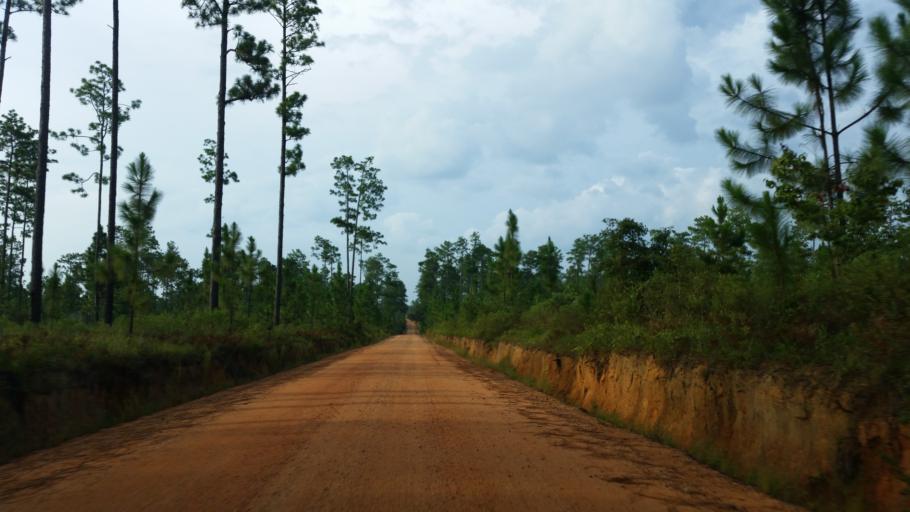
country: US
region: Alabama
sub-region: Escambia County
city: Atmore
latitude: 30.8698
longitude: -87.5820
